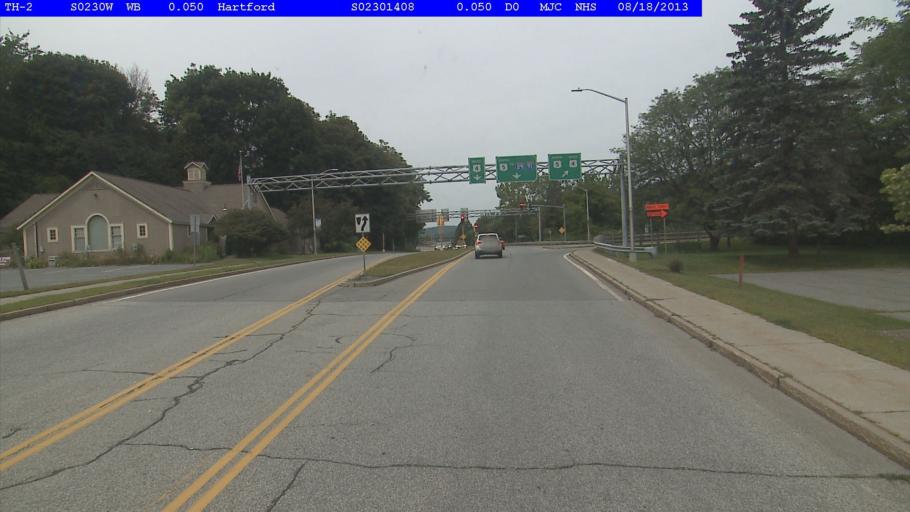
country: US
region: Vermont
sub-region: Windsor County
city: White River Junction
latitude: 43.6504
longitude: -72.3227
